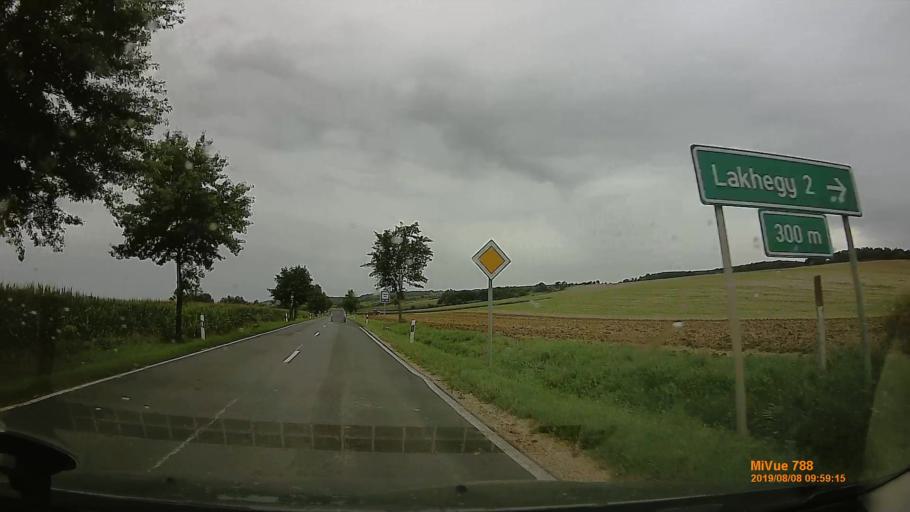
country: HU
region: Vas
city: Vasvar
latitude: 46.9724
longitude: 16.8428
